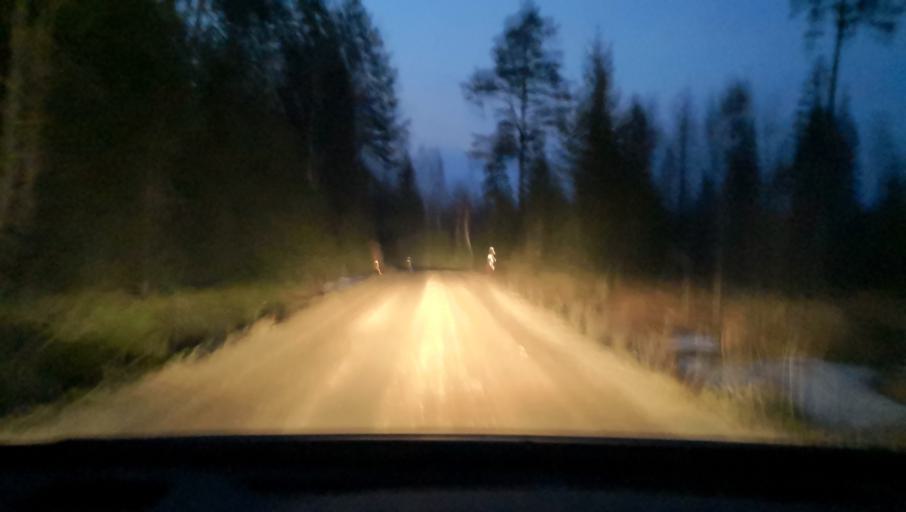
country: SE
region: OErebro
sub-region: Lindesbergs Kommun
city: Frovi
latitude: 59.6227
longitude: 15.4805
